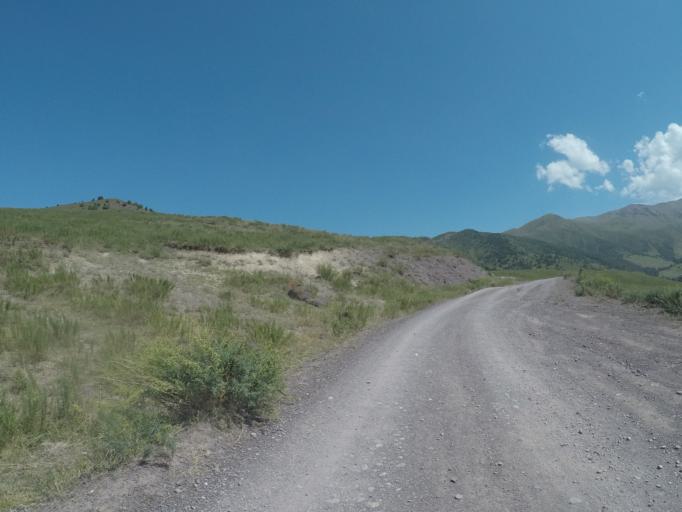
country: KG
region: Chuy
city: Bishkek
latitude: 42.6473
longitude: 74.5223
